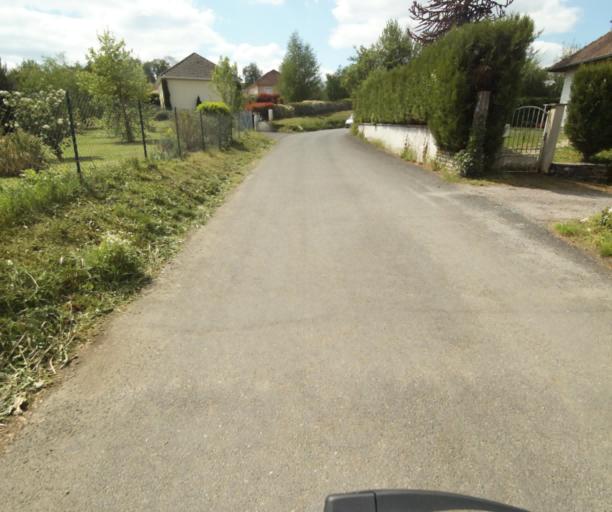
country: FR
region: Limousin
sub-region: Departement de la Correze
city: Tulle
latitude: 45.2834
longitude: 1.7752
